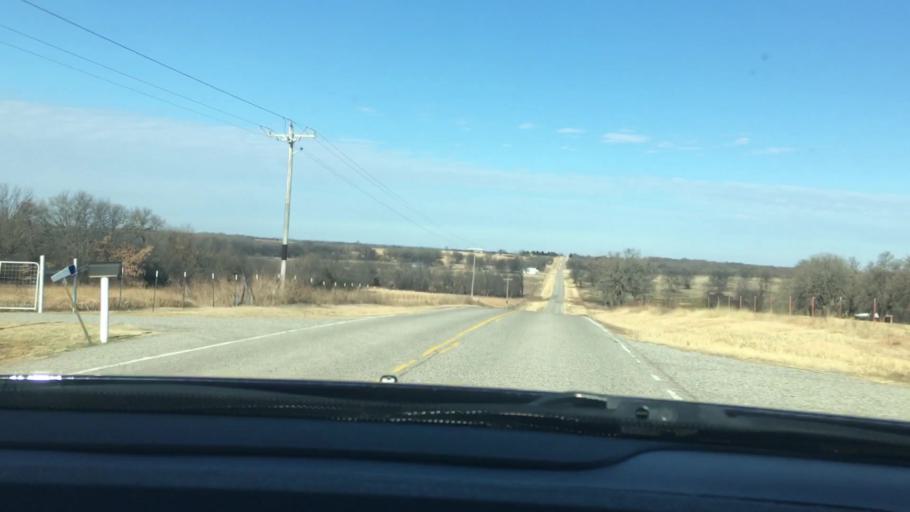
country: US
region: Oklahoma
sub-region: Garvin County
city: Wynnewood
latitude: 34.6732
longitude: -97.1254
